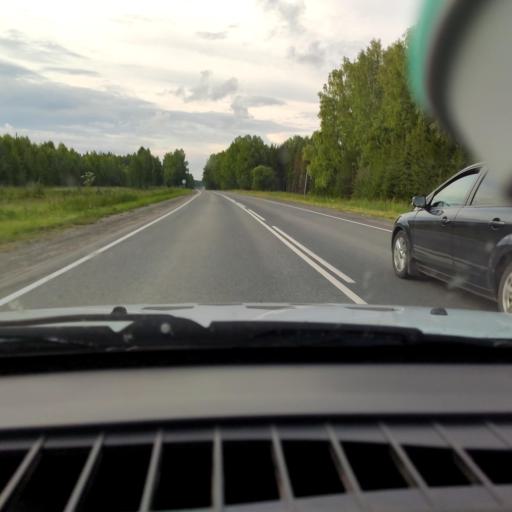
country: RU
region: Perm
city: Orda
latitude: 57.2485
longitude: 56.9967
